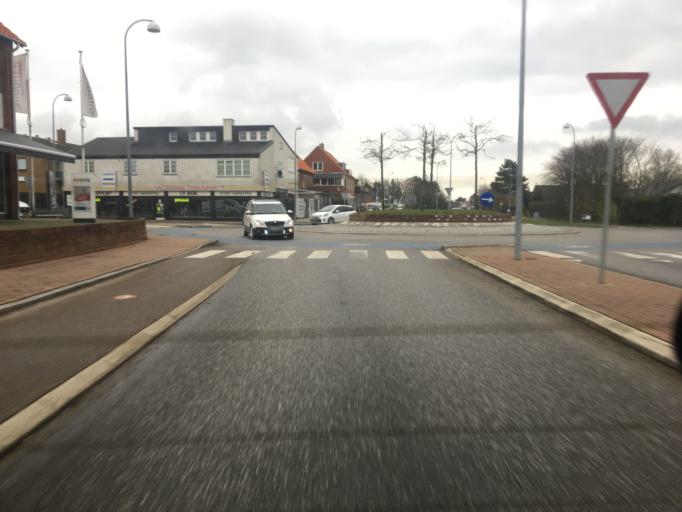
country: DK
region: Capital Region
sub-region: Vallensbaek Kommune
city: Vallensbaek
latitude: 55.6179
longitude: 12.3830
